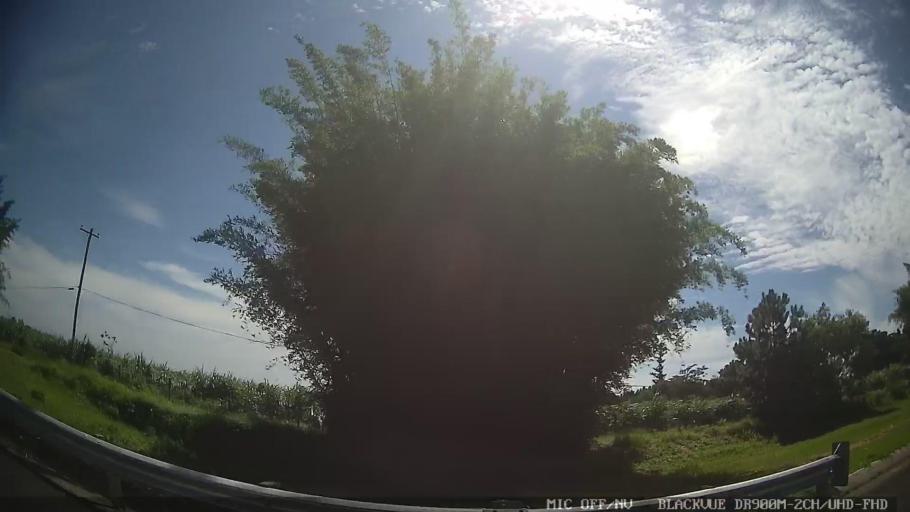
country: BR
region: Sao Paulo
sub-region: Cerquilho
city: Cerquilho
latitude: -23.1758
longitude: -47.6412
